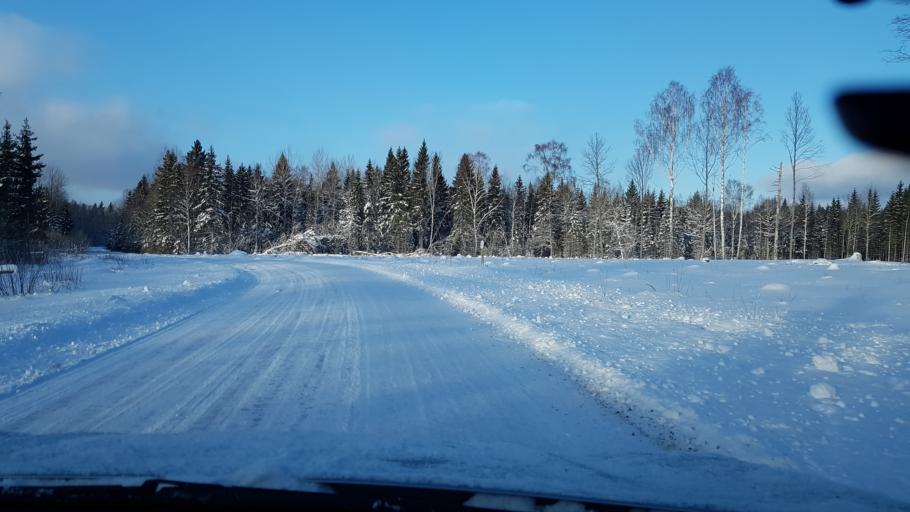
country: EE
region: Harju
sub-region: Nissi vald
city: Turba
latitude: 59.1182
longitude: 24.2213
